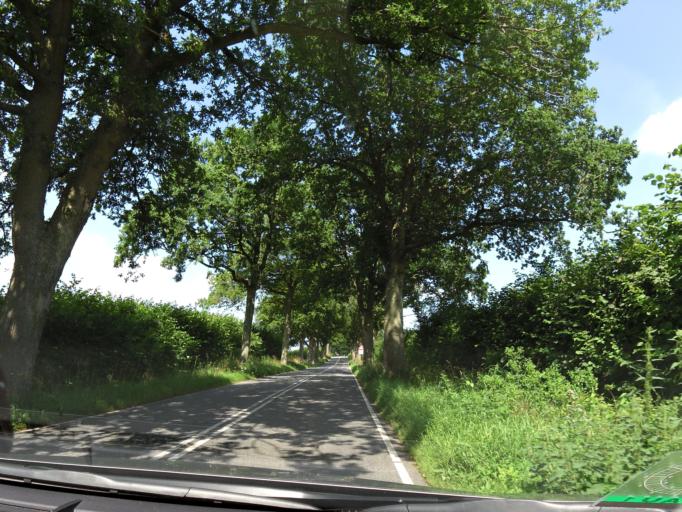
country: DK
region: South Denmark
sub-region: Assens Kommune
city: Arup
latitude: 55.3867
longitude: 10.0503
